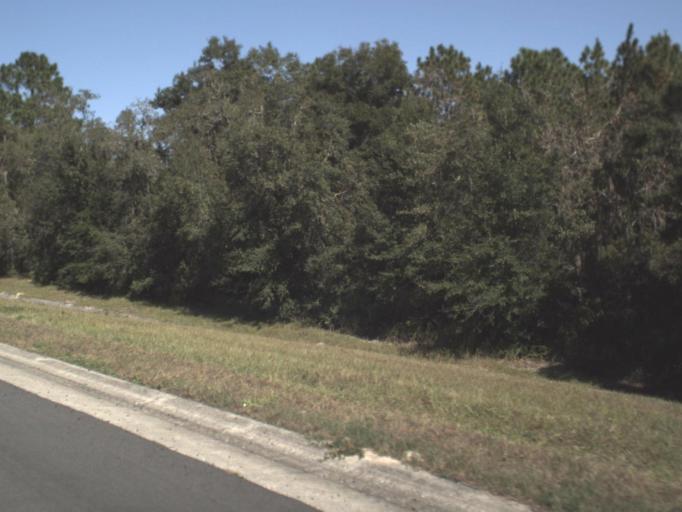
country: US
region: Florida
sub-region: Hernando County
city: Brookridge
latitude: 28.5995
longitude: -82.4895
